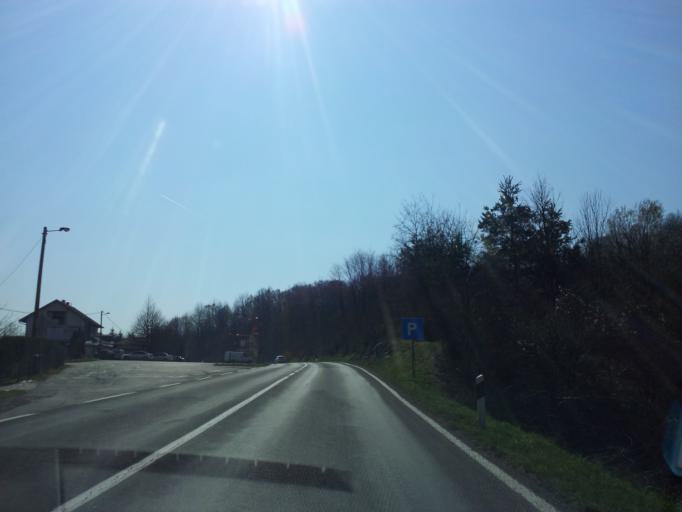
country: HR
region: Karlovacka
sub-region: Grad Karlovac
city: Slunj
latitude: 45.1017
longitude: 15.5888
